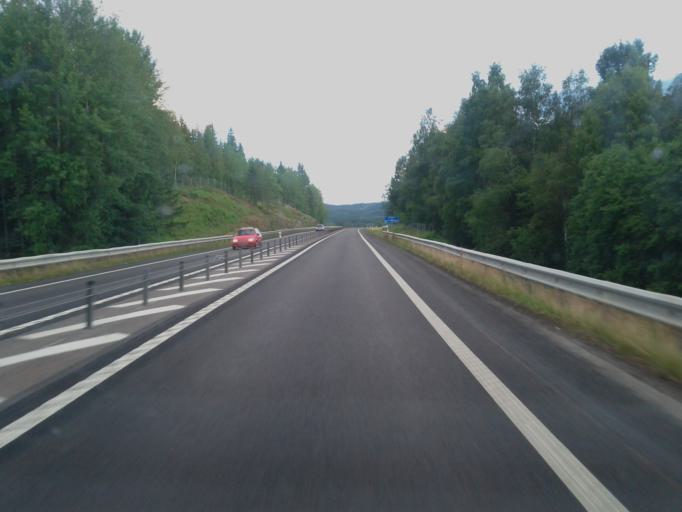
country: SE
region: Dalarna
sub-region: Borlange Kommun
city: Borlaenge
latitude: 60.4313
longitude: 15.3392
